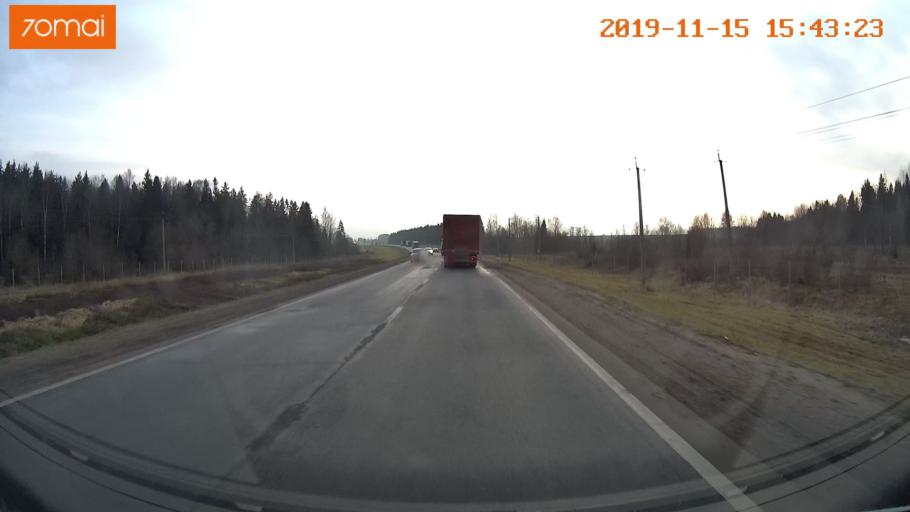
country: RU
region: Jaroslavl
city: Danilov
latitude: 57.9830
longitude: 40.0284
